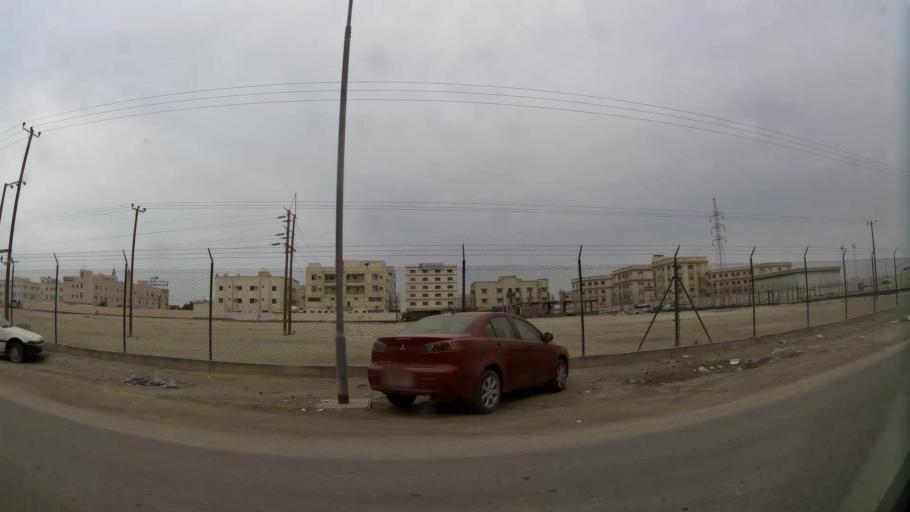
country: BH
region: Northern
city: Madinat `Isa
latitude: 26.1809
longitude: 50.5346
